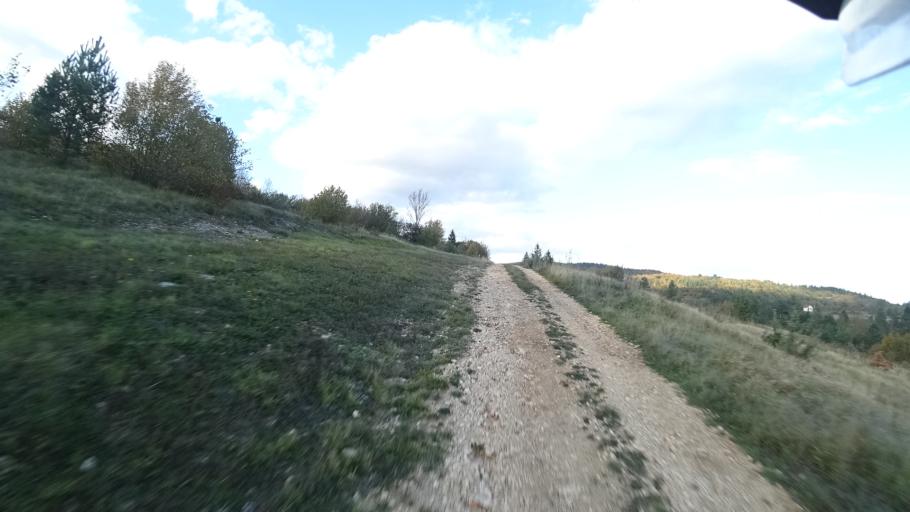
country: HR
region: Karlovacka
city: Plaski
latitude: 44.9992
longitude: 15.4244
